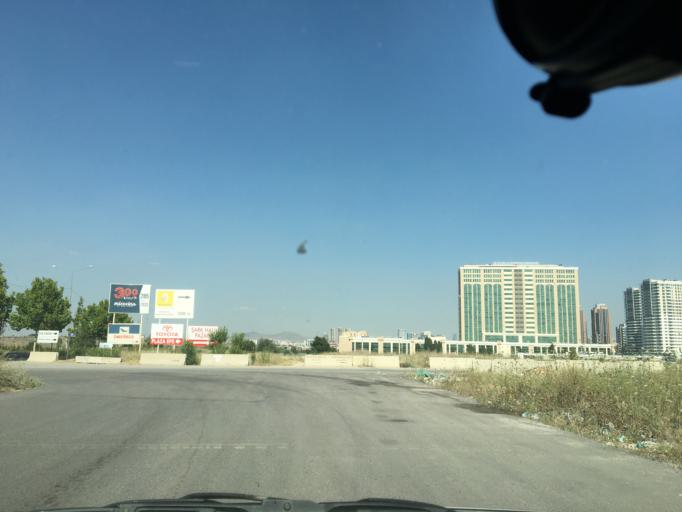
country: TR
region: Ankara
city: Batikent
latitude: 39.9124
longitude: 32.7456
